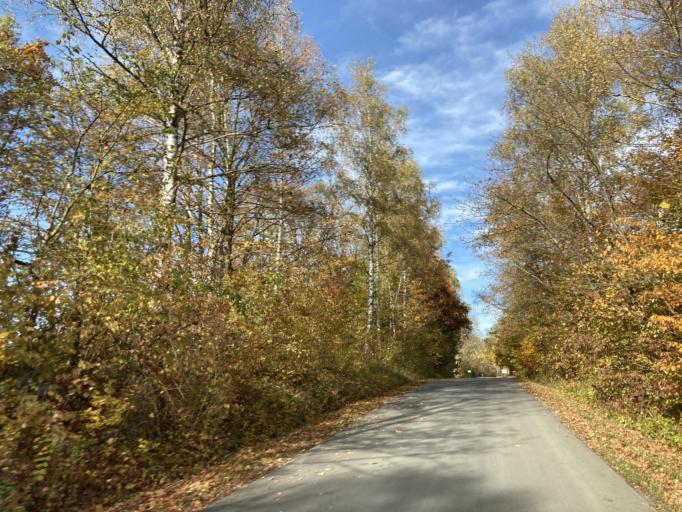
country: DE
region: Baden-Wuerttemberg
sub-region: Tuebingen Region
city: Rottenburg
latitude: 48.4558
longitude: 8.9428
